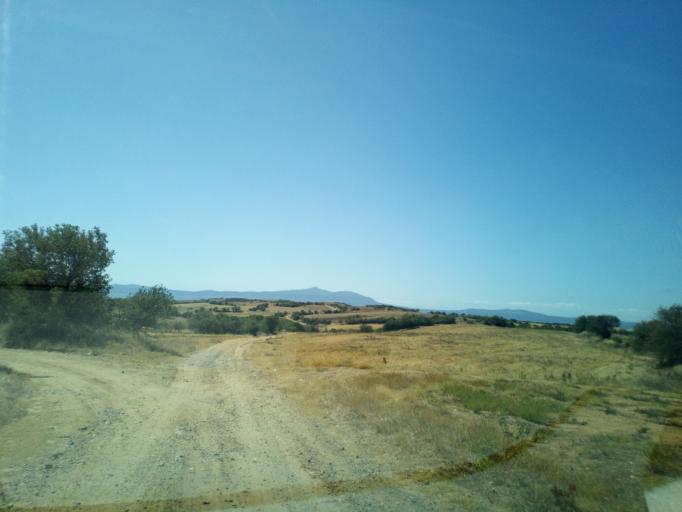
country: GR
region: Central Macedonia
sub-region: Nomos Thessalonikis
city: Kolchikon
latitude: 40.7452
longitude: 23.2511
